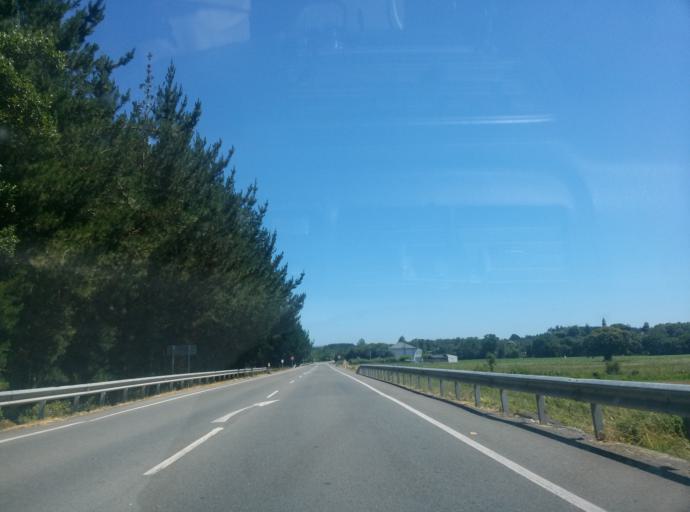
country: ES
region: Galicia
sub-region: Provincia de Lugo
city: Castro de Rei
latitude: 43.2492
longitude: -7.4184
